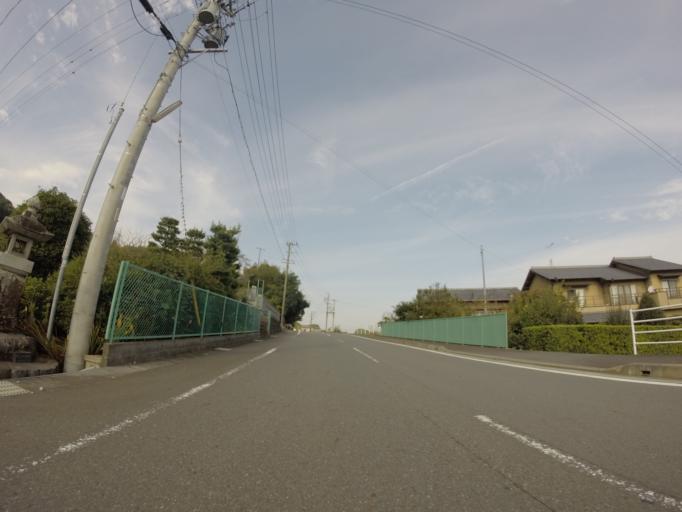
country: JP
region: Shizuoka
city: Shimada
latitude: 34.7680
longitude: 138.1817
